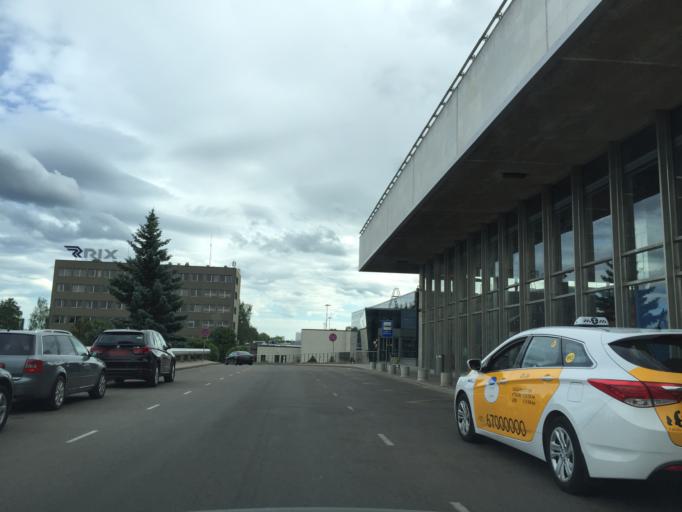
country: LV
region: Babite
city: Pinki
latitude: 56.9219
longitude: 23.9798
